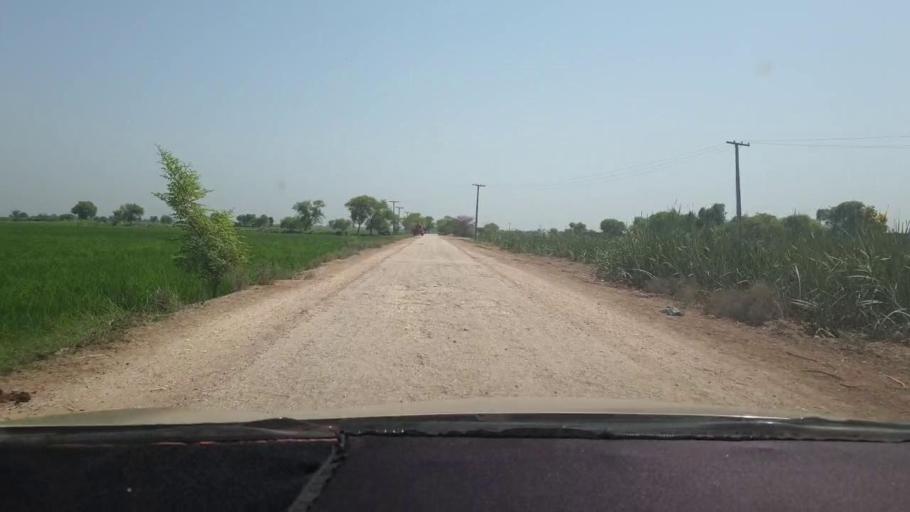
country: PK
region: Sindh
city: Miro Khan
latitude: 27.6829
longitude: 68.0950
